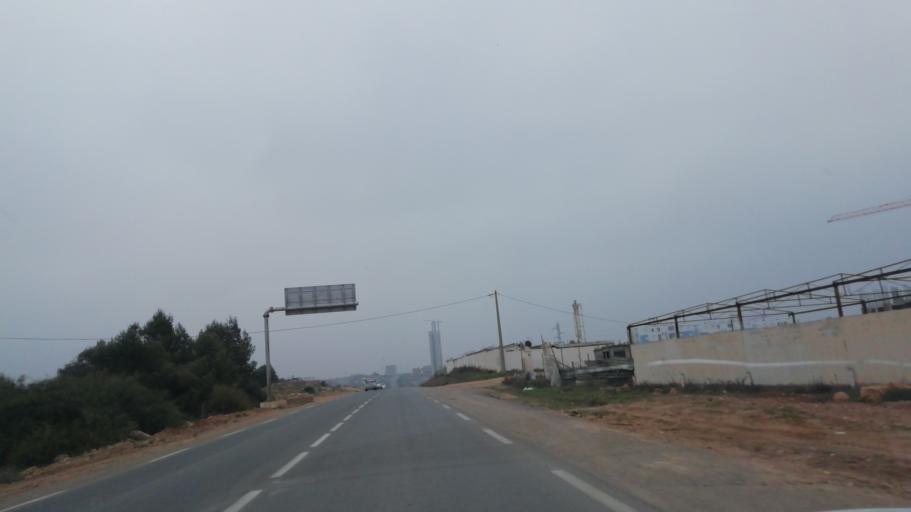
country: DZ
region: Mascara
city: Mascara
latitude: 35.4198
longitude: 0.1328
